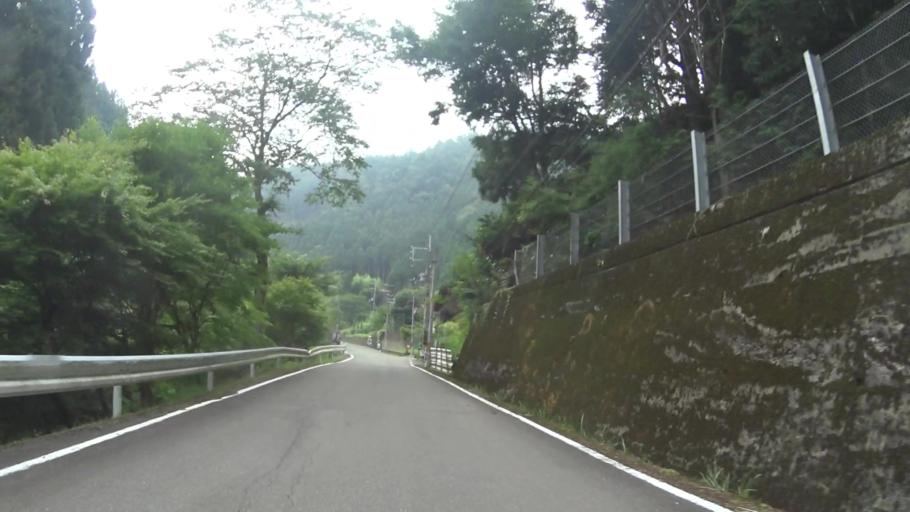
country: JP
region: Kyoto
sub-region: Kyoto-shi
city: Kamigyo-ku
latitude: 35.1903
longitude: 135.7372
